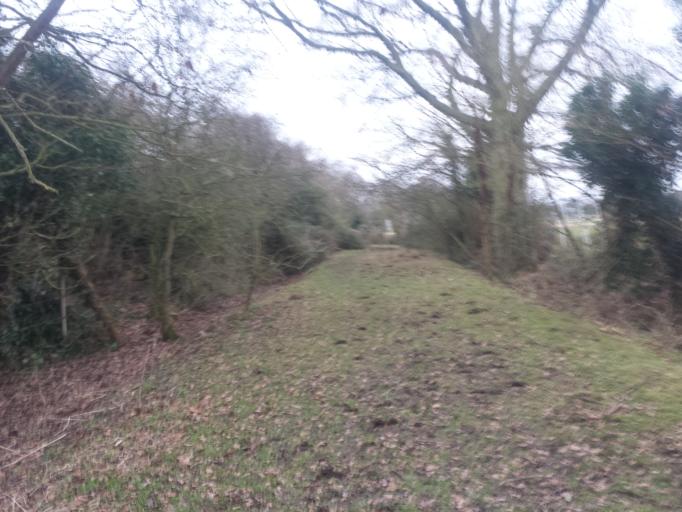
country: GB
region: England
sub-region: Essex
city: Little Clacton
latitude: 51.8427
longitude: 1.1421
